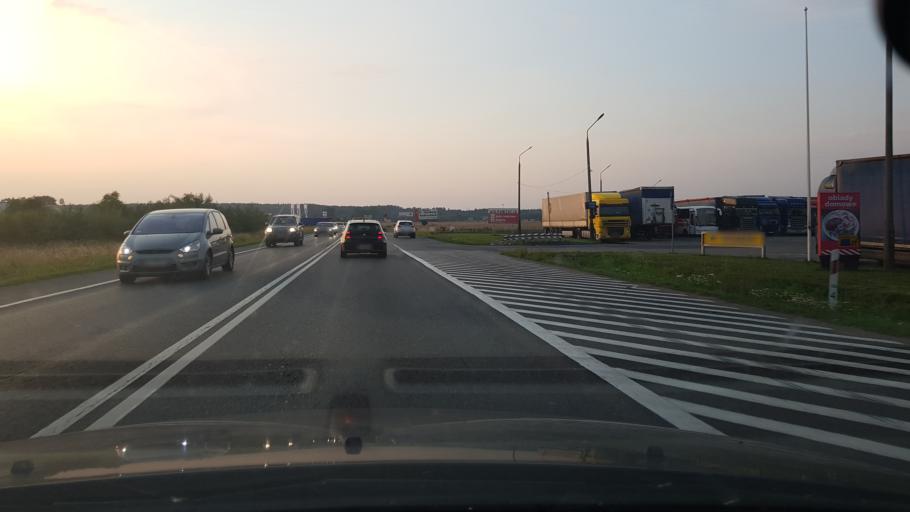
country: PL
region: Masovian Voivodeship
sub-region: Powiat mlawski
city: Mlawa
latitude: 53.1169
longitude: 20.3977
